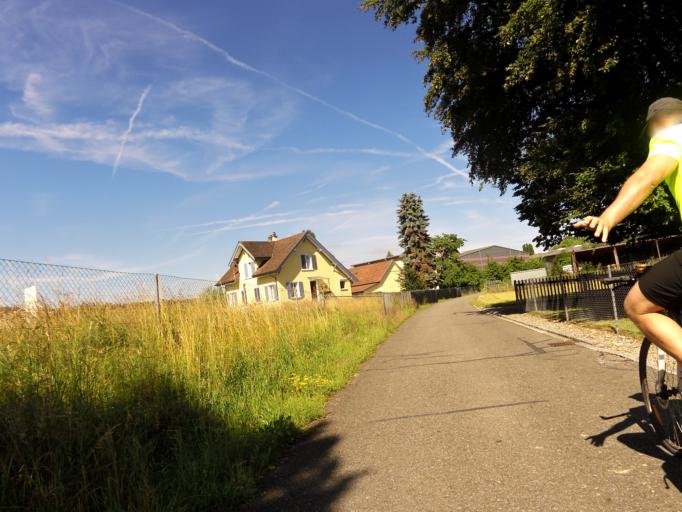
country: CH
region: Thurgau
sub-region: Kreuzlingen District
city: Kreuzlingen
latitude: 47.6462
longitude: 9.1922
